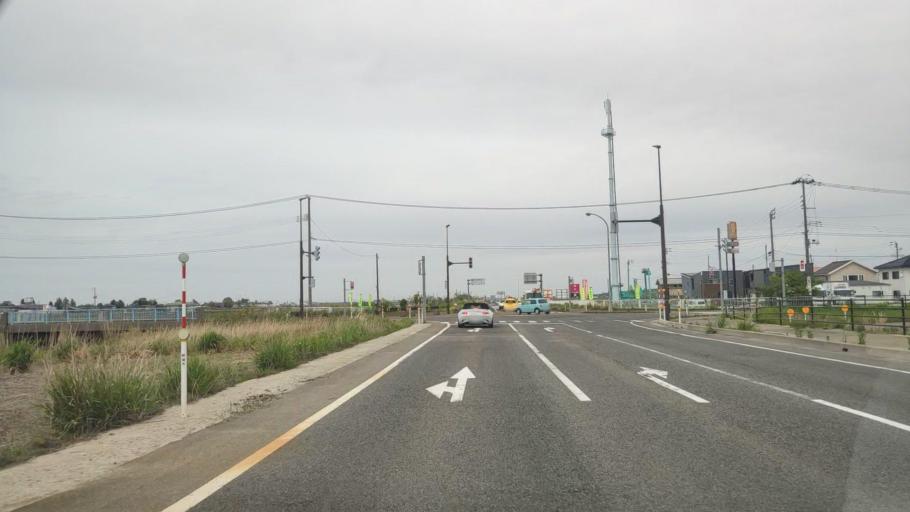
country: JP
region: Niigata
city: Niitsu-honcho
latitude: 37.7505
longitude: 139.0872
